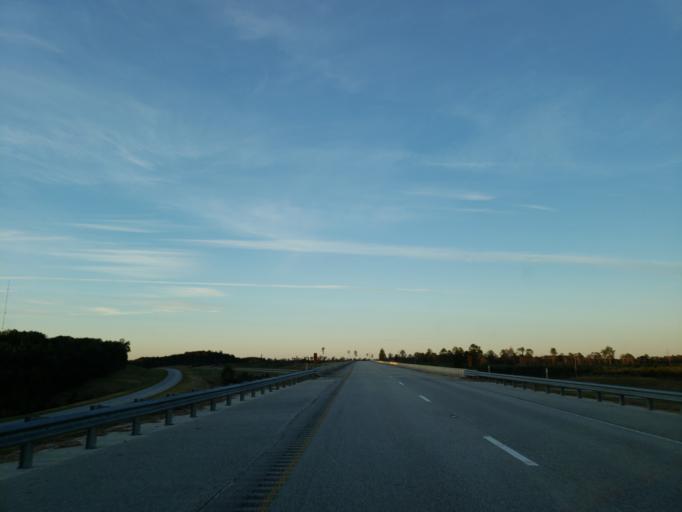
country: US
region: Mississippi
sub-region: Wayne County
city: Belmont
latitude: 31.4512
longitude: -88.4647
